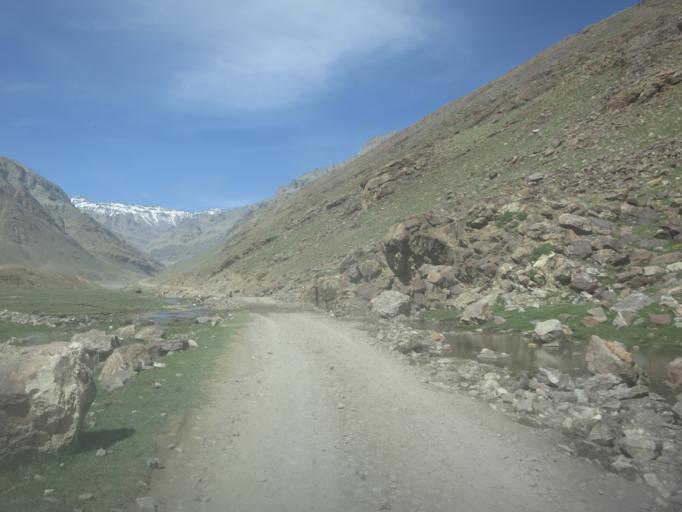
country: IN
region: Himachal Pradesh
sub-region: Kulu
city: Manali
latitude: 32.4442
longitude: 77.6898
